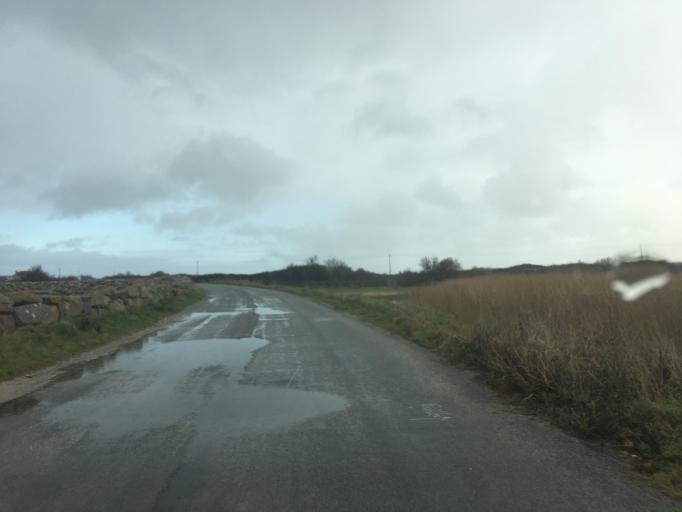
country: FR
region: Lower Normandy
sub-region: Departement de la Manche
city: Reville
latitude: 49.6937
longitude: -1.2742
